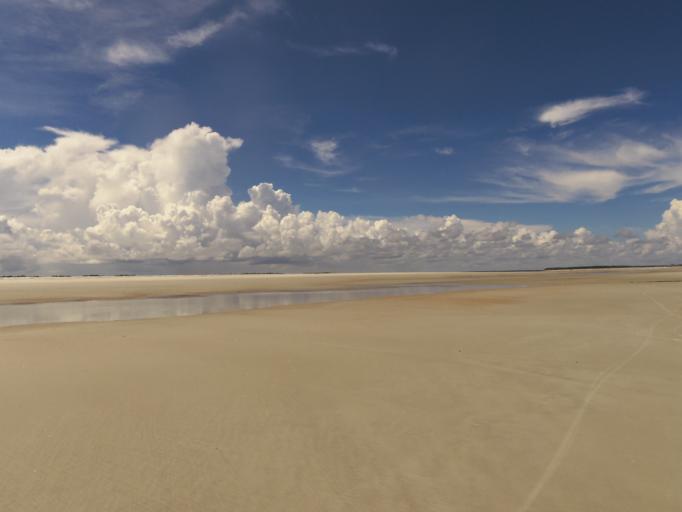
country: US
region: Florida
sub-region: Duval County
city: Atlantic Beach
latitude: 30.4857
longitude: -81.4156
